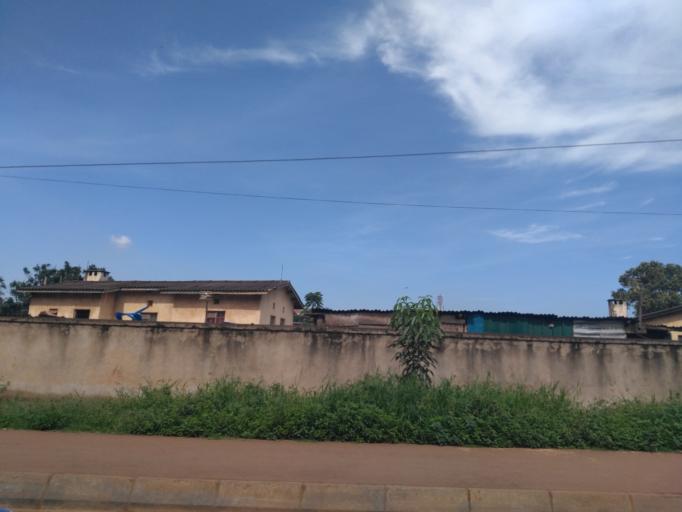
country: UG
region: Central Region
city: Kampala Central Division
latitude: 0.3302
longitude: 32.5753
